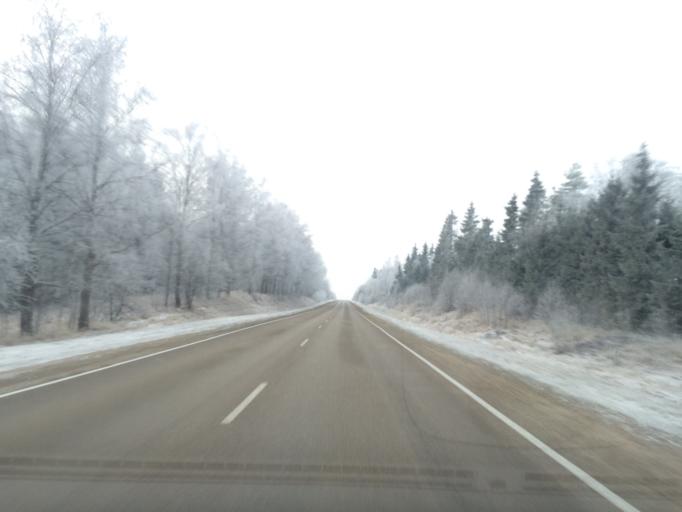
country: LV
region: Rezekne
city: Rezekne
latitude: 56.6231
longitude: 27.4569
